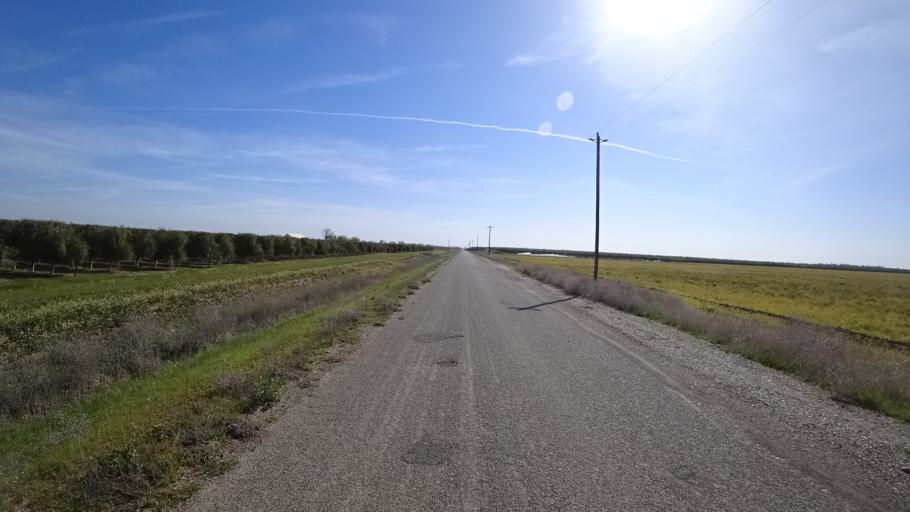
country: US
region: California
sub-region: Glenn County
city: Willows
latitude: 39.6114
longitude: -122.2273
